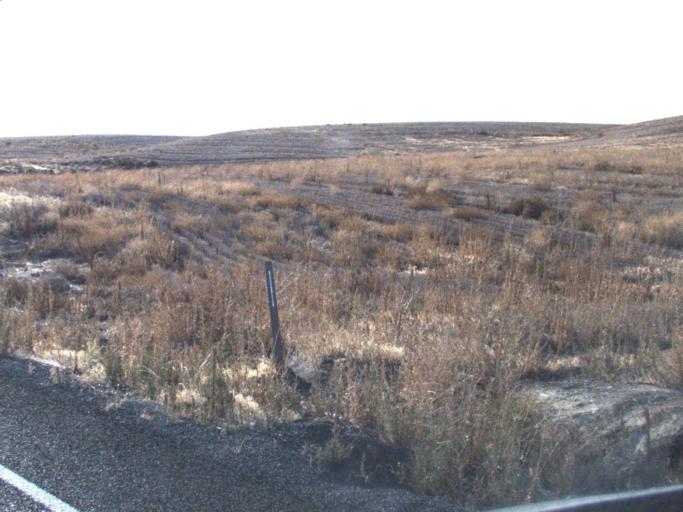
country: US
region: Washington
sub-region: Franklin County
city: Connell
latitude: 46.6335
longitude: -118.7591
